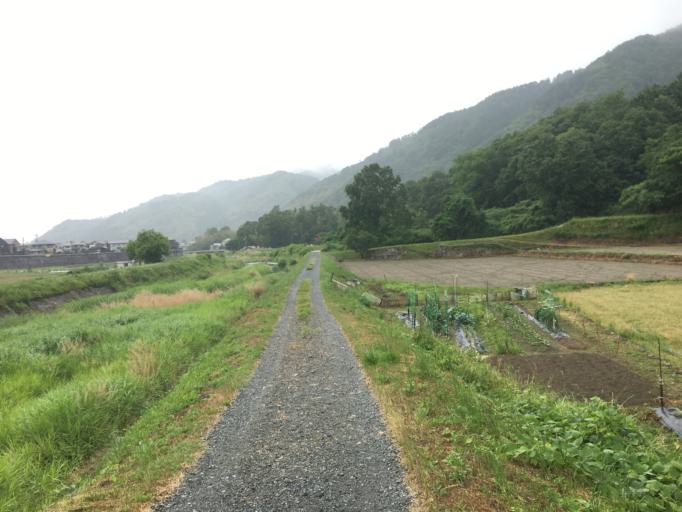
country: JP
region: Kyoto
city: Kameoka
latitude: 35.0066
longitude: 135.6128
